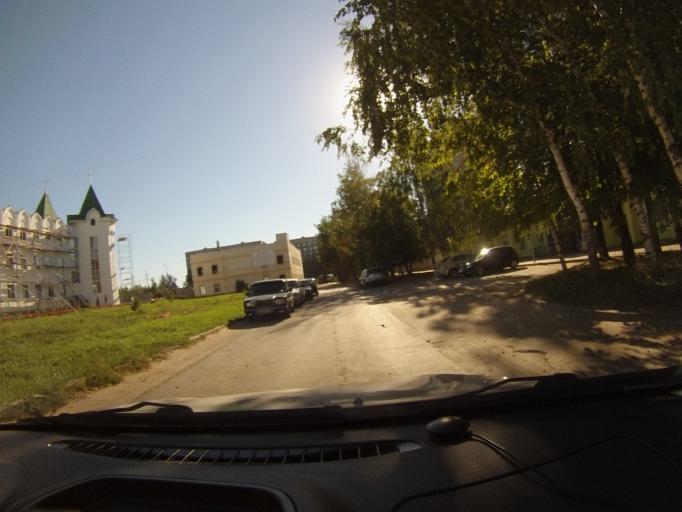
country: RU
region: Tambov
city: Tambov
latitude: 52.7572
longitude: 41.4098
